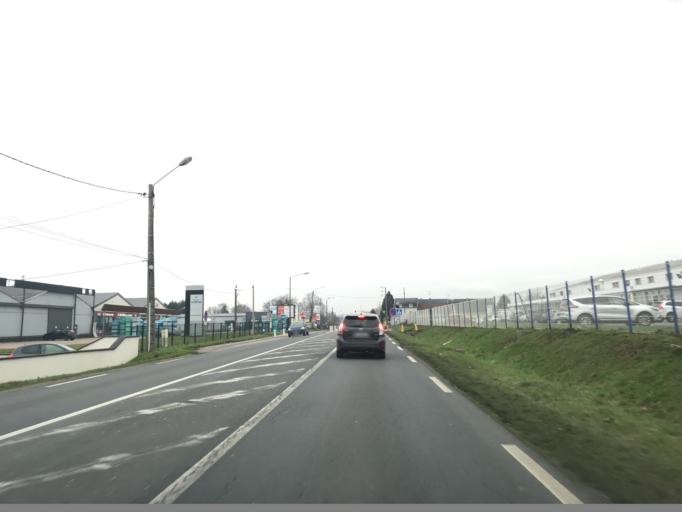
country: FR
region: Haute-Normandie
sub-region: Departement de la Seine-Maritime
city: Boos
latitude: 49.3969
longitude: 1.1803
